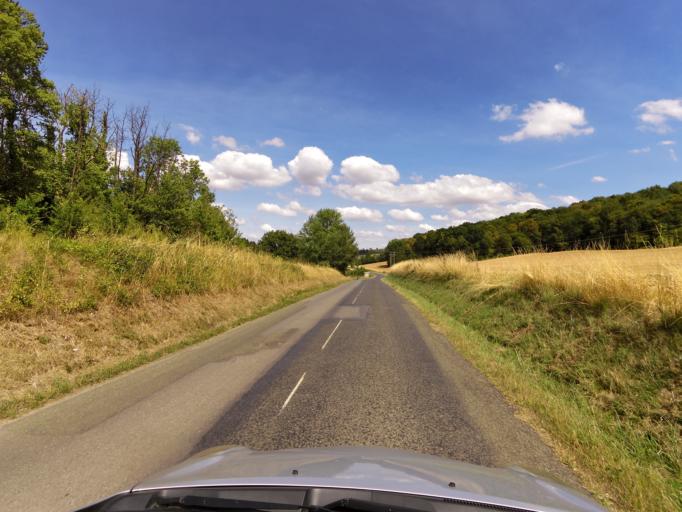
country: FR
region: Picardie
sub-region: Departement de l'Aisne
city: Courmelles
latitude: 49.3379
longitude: 3.3070
